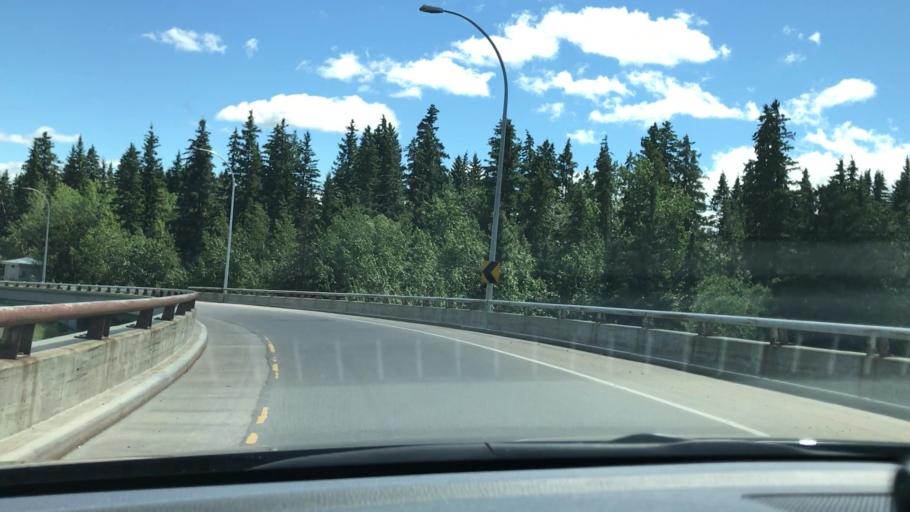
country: CA
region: Alberta
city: Edmonton
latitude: 53.5123
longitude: -113.5794
